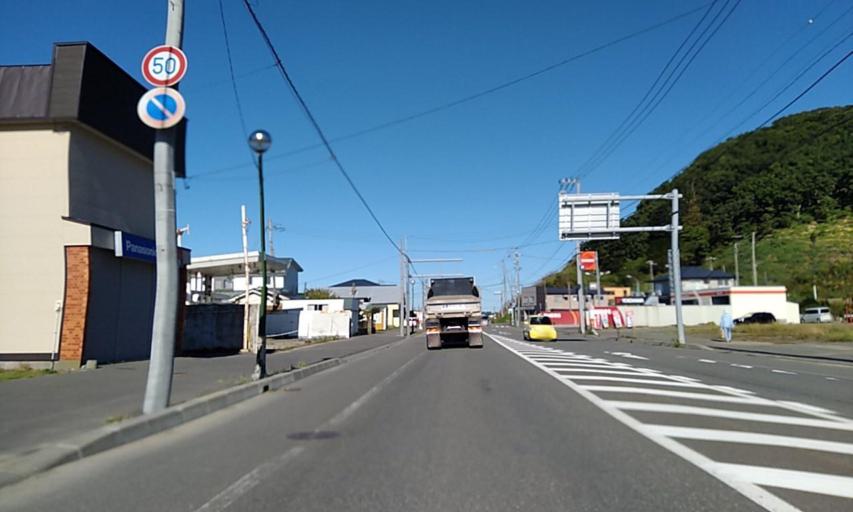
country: JP
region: Hokkaido
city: Shizunai-furukawacho
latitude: 42.4261
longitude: 142.2227
